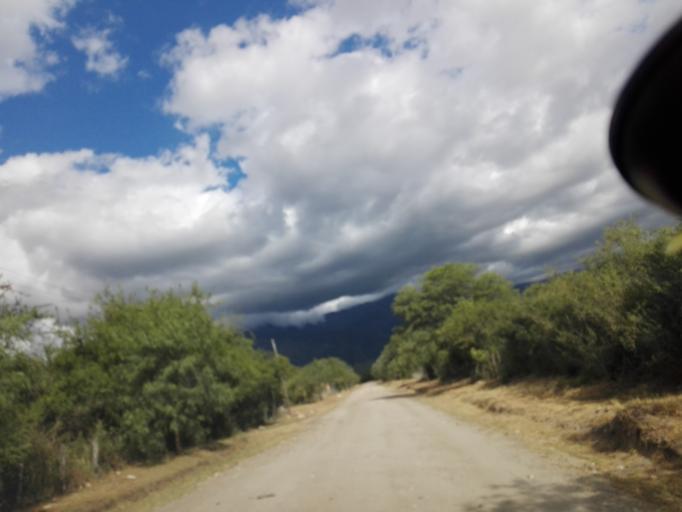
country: AR
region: Cordoba
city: Villa Las Rosas
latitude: -31.9495
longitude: -65.0417
